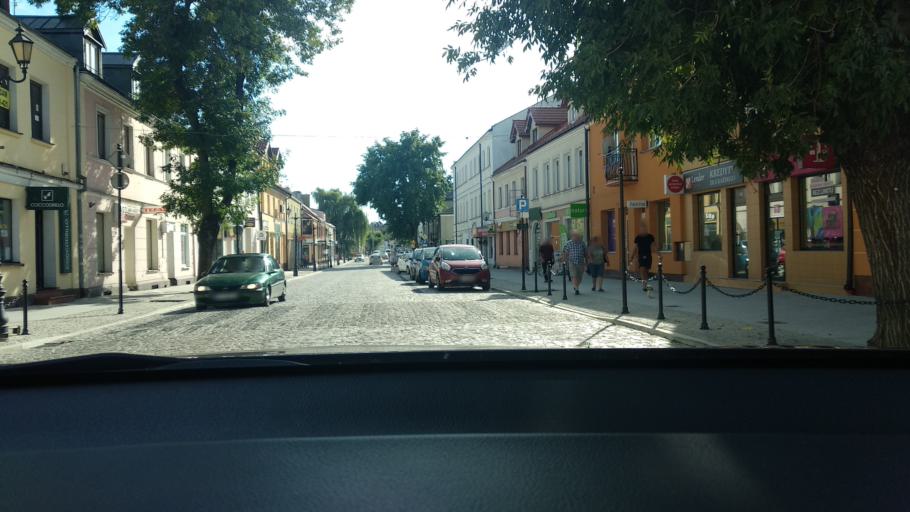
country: PL
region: Masovian Voivodeship
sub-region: Powiat pultuski
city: Pultusk
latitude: 52.7058
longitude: 21.0896
